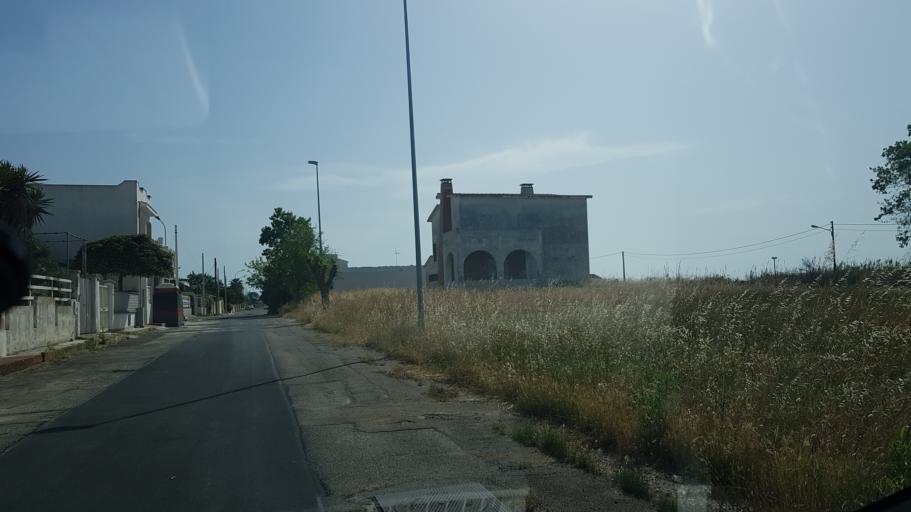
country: IT
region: Apulia
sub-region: Provincia di Brindisi
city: Torchiarolo
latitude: 40.5315
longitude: 18.0767
